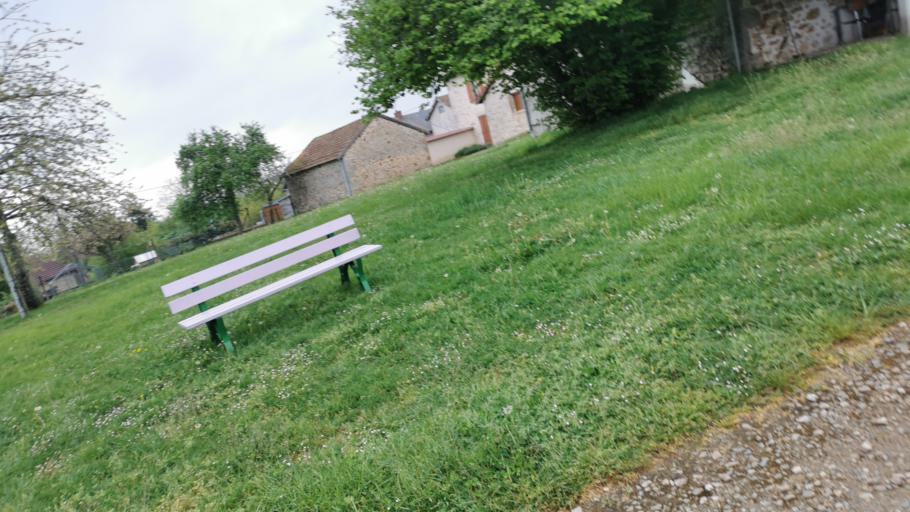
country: FR
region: Limousin
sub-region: Departement de la Creuse
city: Bourganeuf
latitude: 45.9516
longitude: 1.6812
